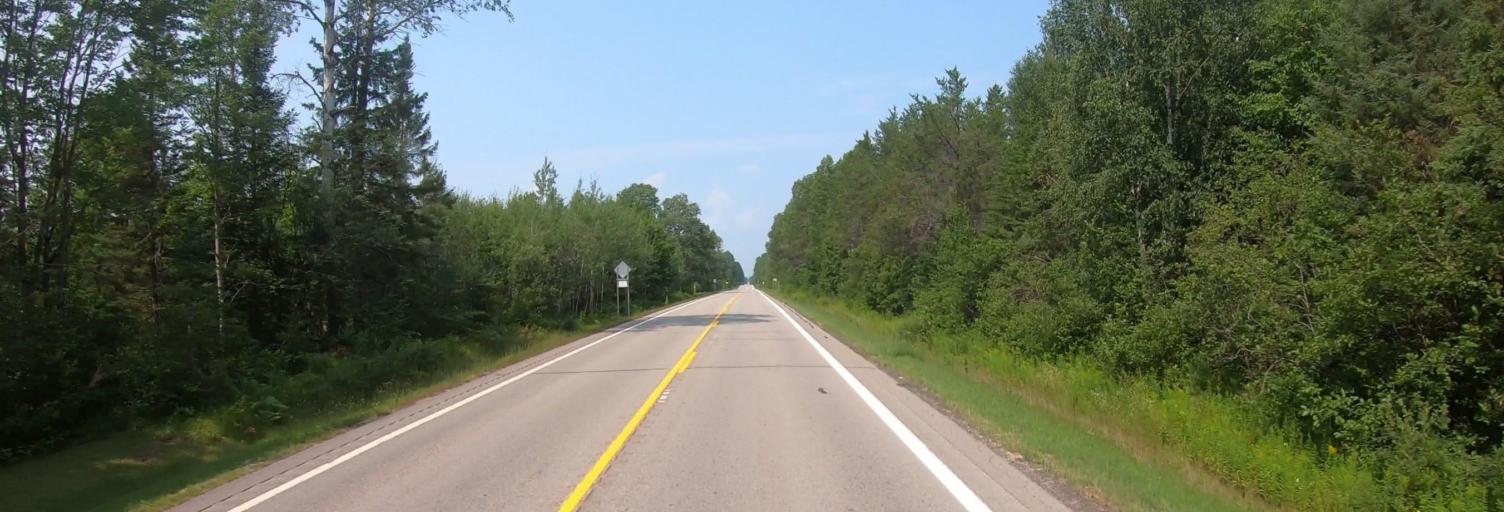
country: US
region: Michigan
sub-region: Luce County
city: Newberry
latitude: 46.5641
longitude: -85.2919
